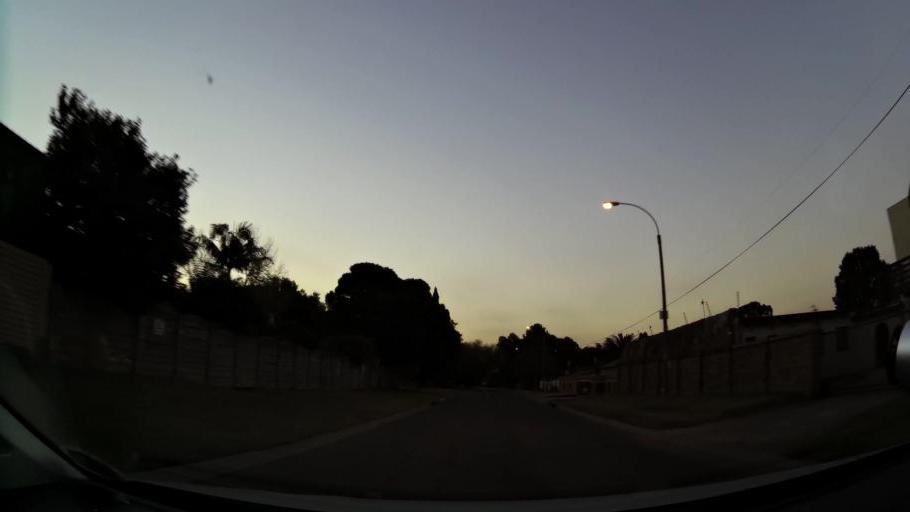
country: ZA
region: Gauteng
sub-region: Ekurhuleni Metropolitan Municipality
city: Tembisa
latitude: -26.0494
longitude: 28.2443
